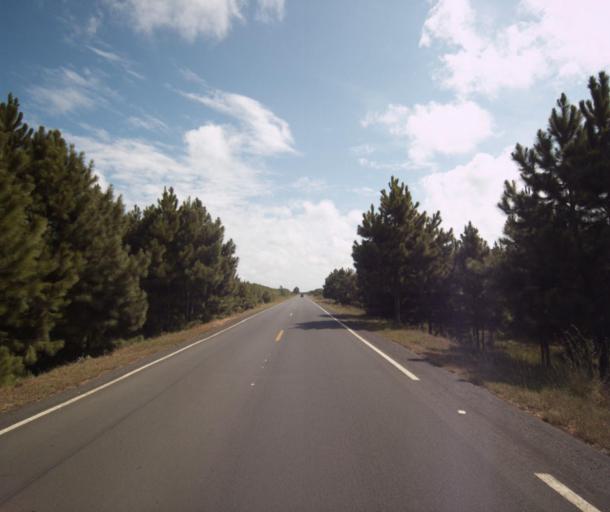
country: BR
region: Rio Grande do Sul
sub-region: Sao Lourenco Do Sul
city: Sao Lourenco do Sul
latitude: -31.4460
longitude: -51.2059
